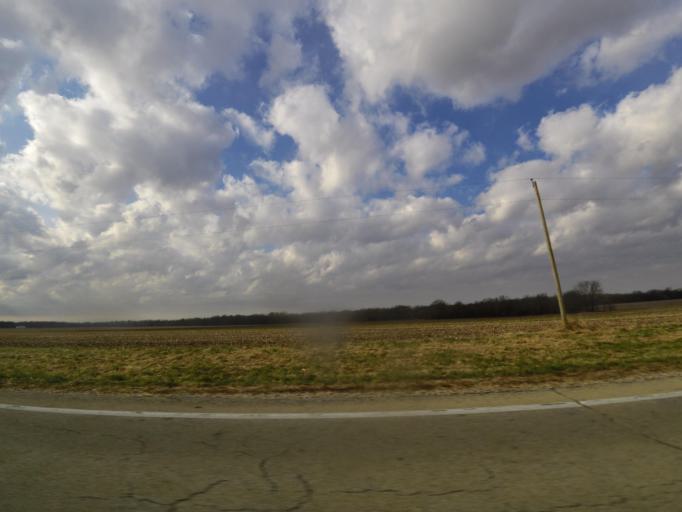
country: US
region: Illinois
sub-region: Fayette County
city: Ramsey
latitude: 39.1902
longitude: -89.1002
